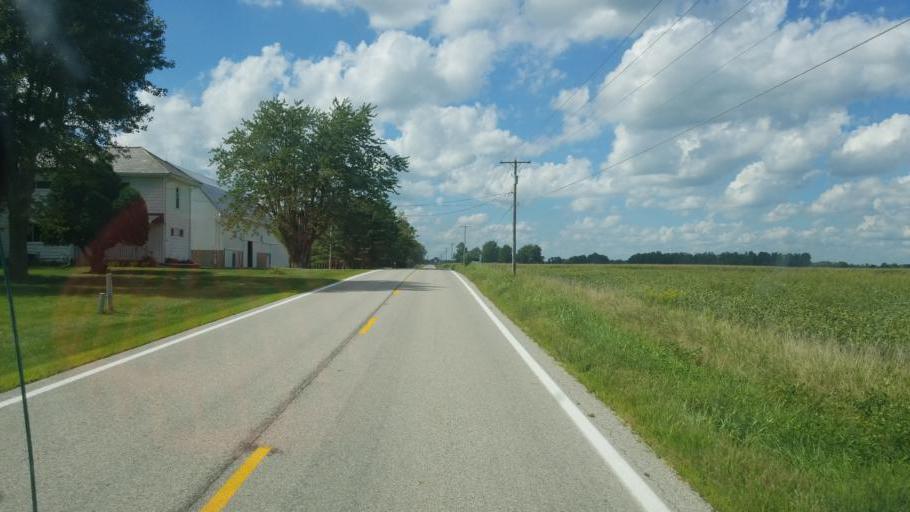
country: US
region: Ohio
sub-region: Union County
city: Richwood
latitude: 40.3712
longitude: -83.2680
